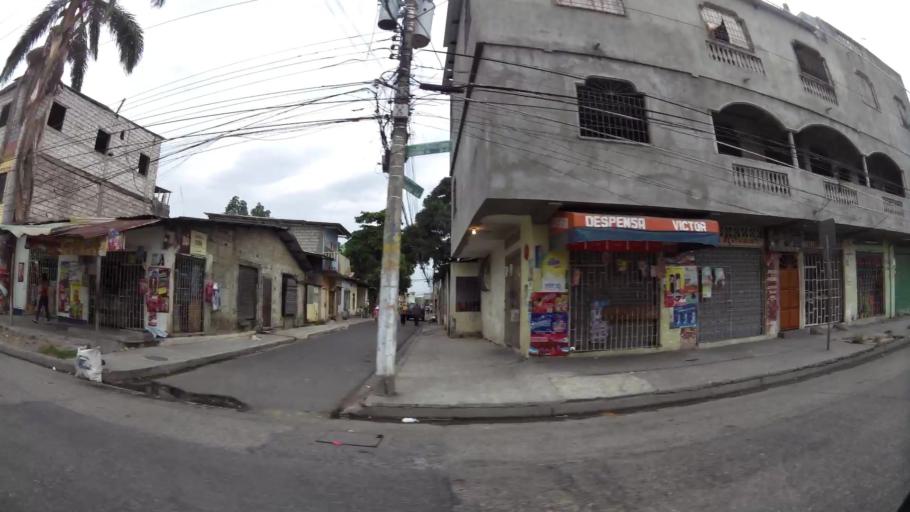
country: EC
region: Guayas
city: Guayaquil
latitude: -2.2481
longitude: -79.8804
